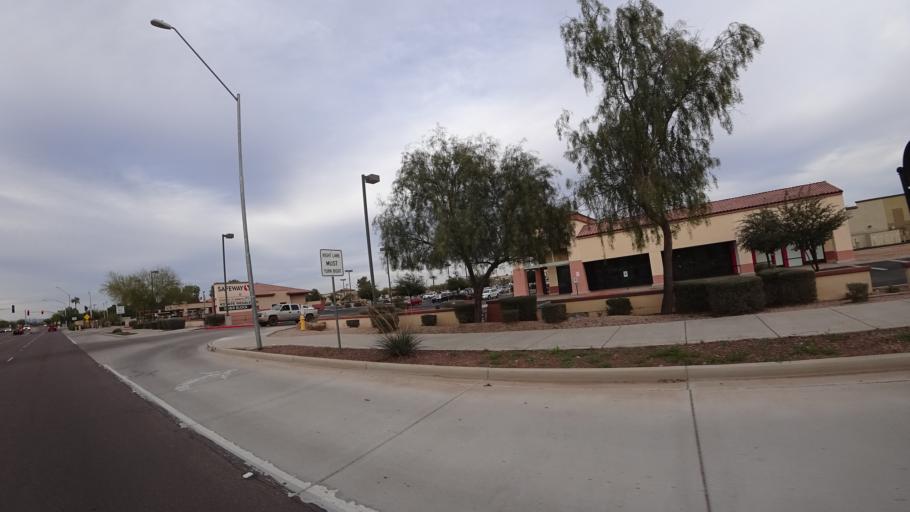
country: US
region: Arizona
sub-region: Maricopa County
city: Sun City West
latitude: 33.6374
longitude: -112.4267
